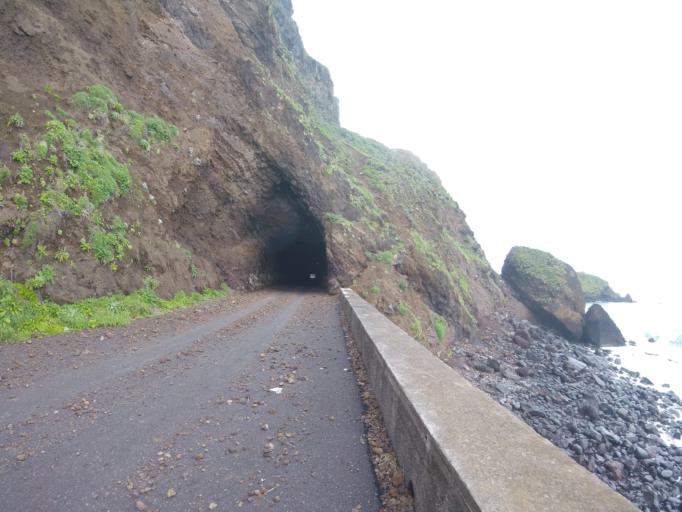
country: PT
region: Madeira
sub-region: Porto Moniz
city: Porto Moniz
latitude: 32.8528
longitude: -17.1505
